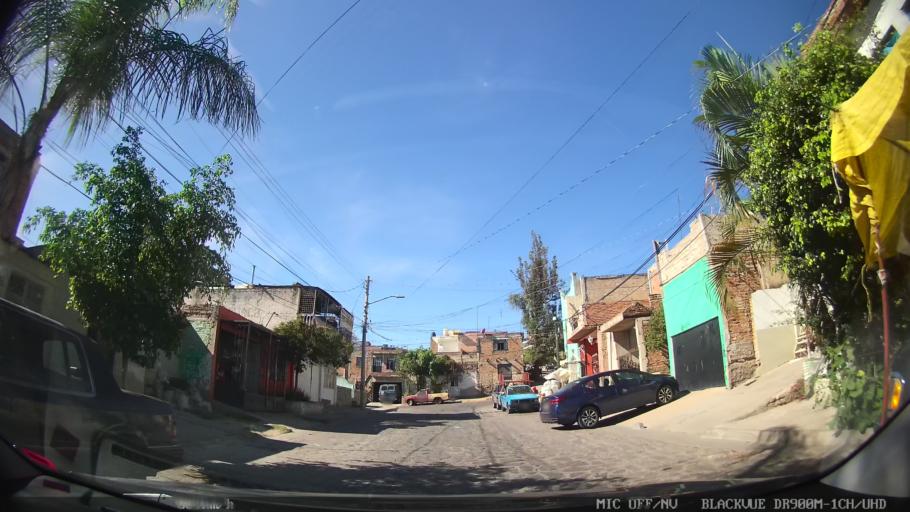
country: MX
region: Jalisco
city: Tlaquepaque
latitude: 20.6869
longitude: -103.2743
